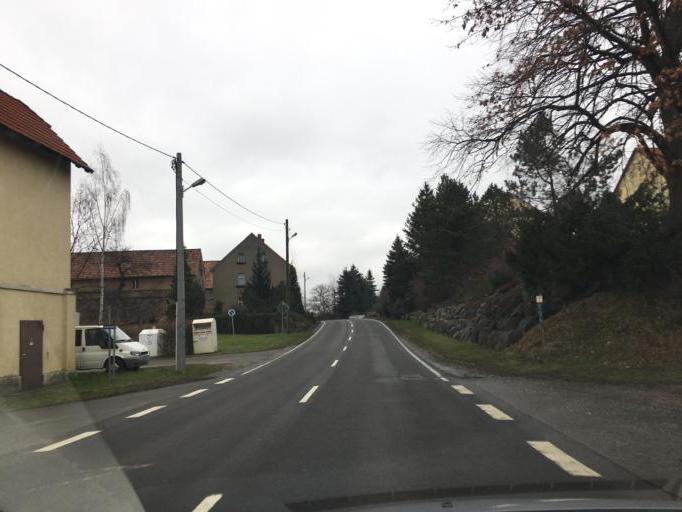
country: DE
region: Thuringia
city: Nobitz
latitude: 50.9510
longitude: 12.5145
